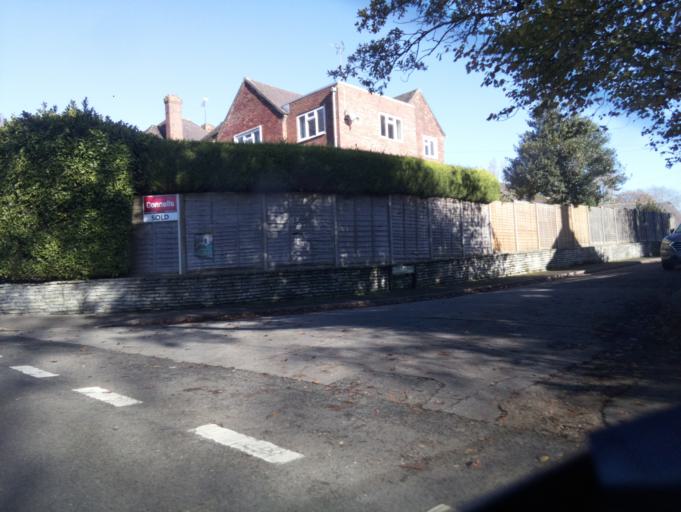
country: GB
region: England
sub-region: Somerset
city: Yeovil
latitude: 50.9498
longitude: -2.6402
